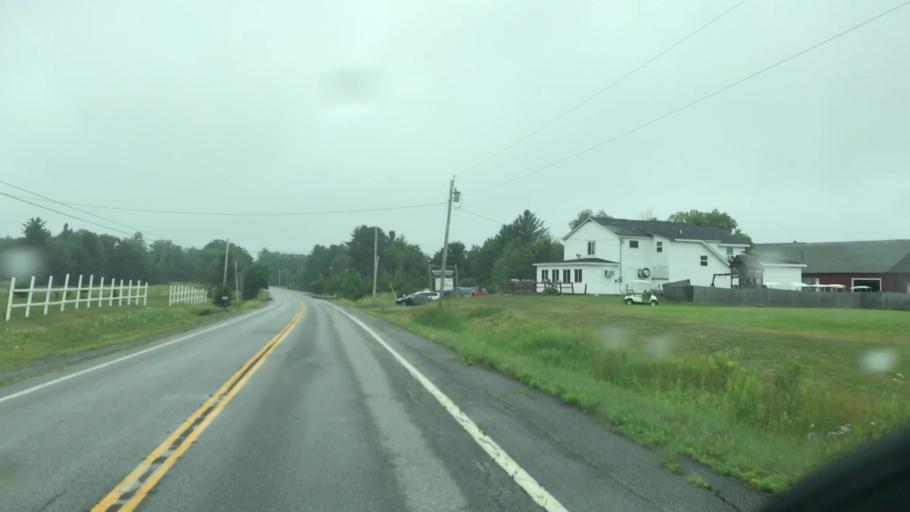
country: US
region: Maine
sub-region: Penobscot County
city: Enfield
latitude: 45.2979
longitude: -68.6191
